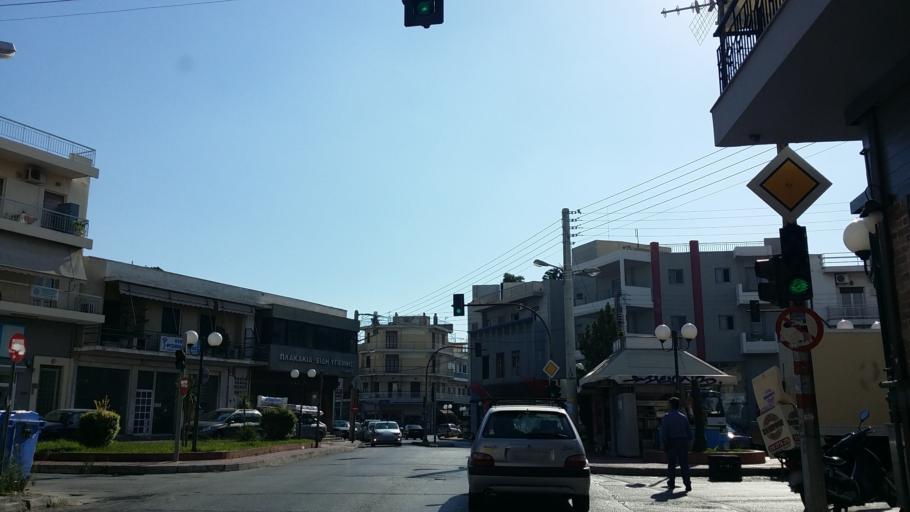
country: GR
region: Attica
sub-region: Nomarchia Athinas
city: Peristeri
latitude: 38.0156
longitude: 23.7078
